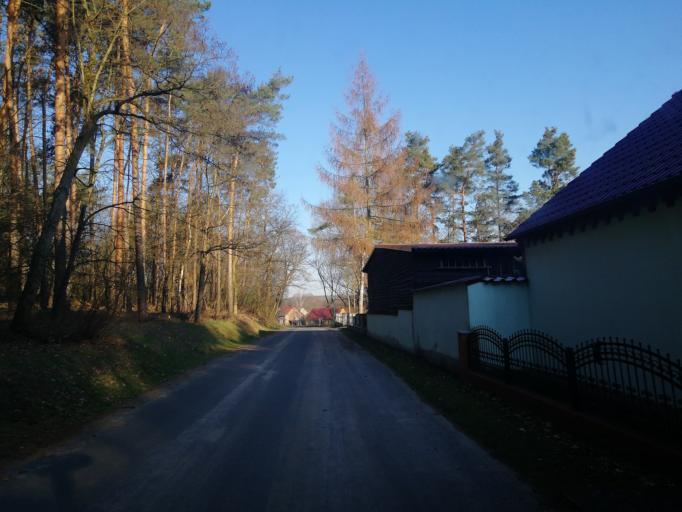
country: DE
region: Brandenburg
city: Drahnsdorf
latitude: 51.9480
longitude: 13.5610
